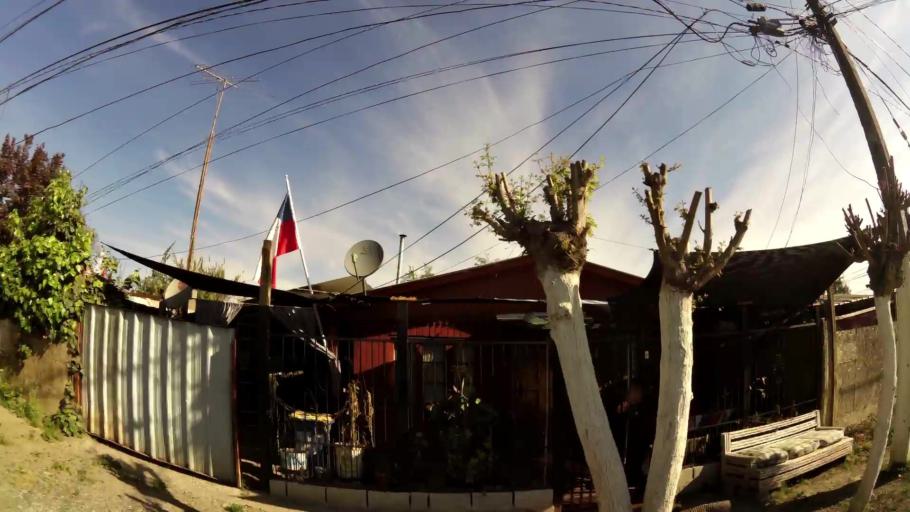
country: CL
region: Santiago Metropolitan
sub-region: Provincia de Santiago
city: Villa Presidente Frei, Nunoa, Santiago, Chile
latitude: -33.5149
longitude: -70.5576
